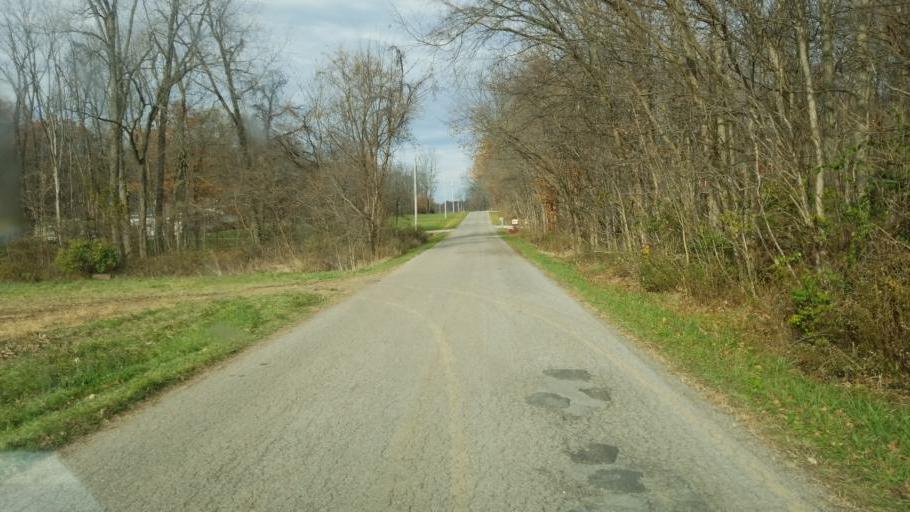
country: US
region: Ohio
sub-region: Morrow County
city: Mount Gilead
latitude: 40.4926
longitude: -82.6933
